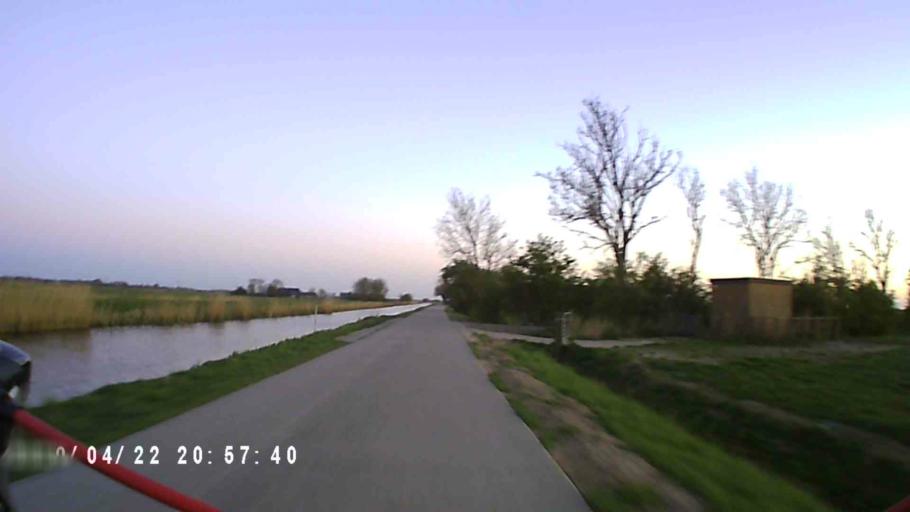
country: NL
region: Groningen
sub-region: Gemeente Winsum
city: Winsum
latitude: 53.3276
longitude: 6.5654
